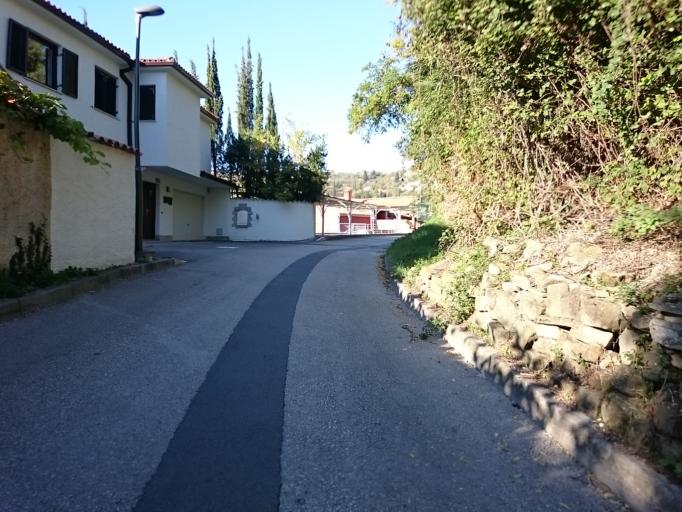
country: SI
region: Piran-Pirano
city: Portoroz
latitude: 45.5128
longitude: 13.5969
